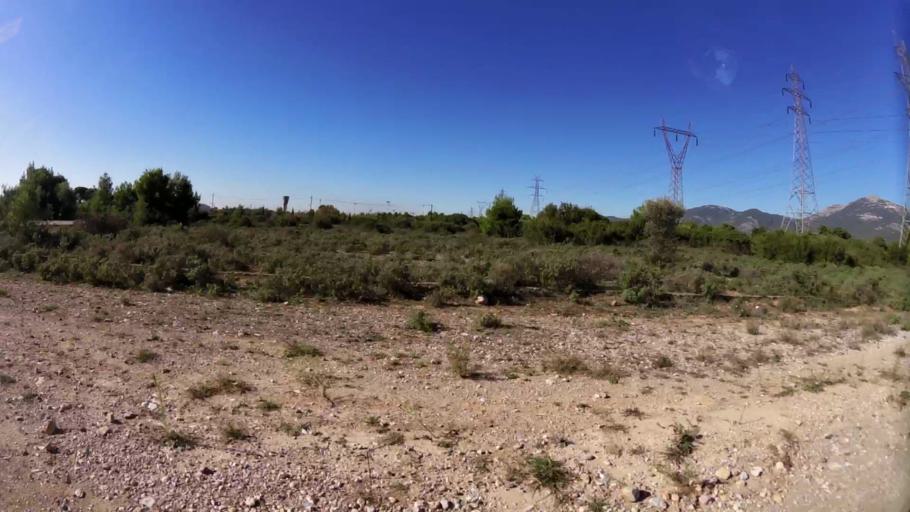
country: GR
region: Attica
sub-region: Nomarchia Anatolikis Attikis
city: Varybobi
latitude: 38.1224
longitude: 23.7795
